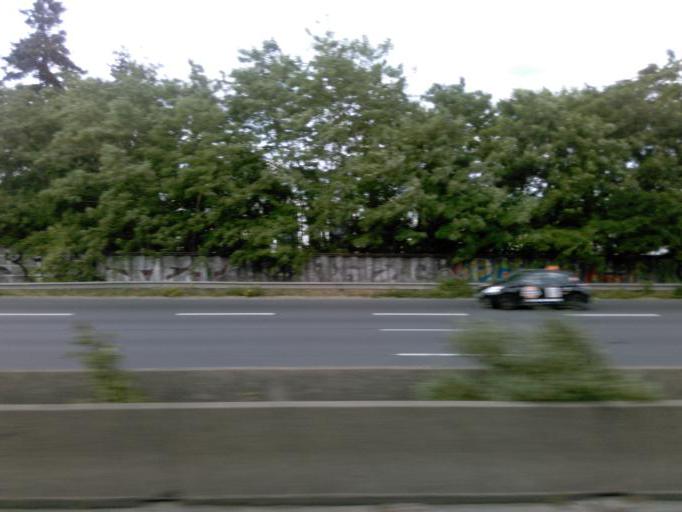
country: FR
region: Ile-de-France
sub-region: Departement du Val-d'Oise
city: Sannois
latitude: 48.9696
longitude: 2.2501
